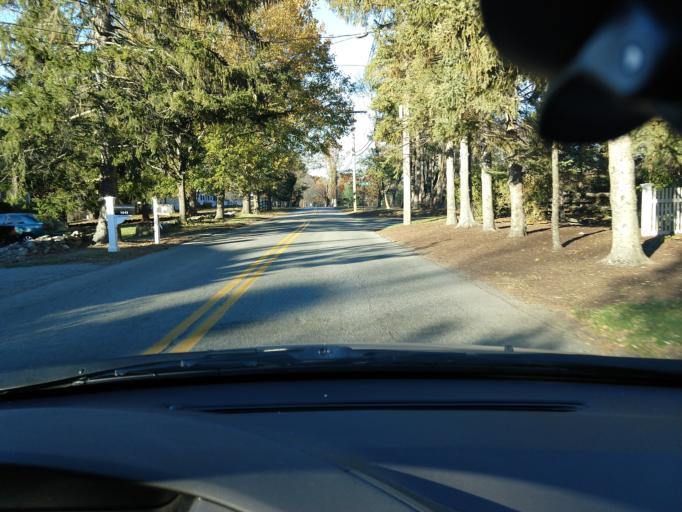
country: US
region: Massachusetts
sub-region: Middlesex County
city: Carlisle
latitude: 42.4996
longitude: -71.3316
